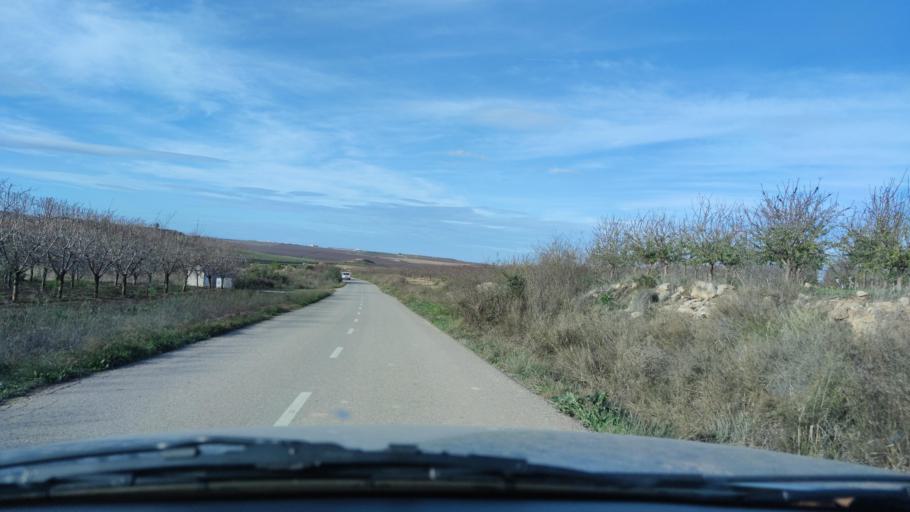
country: ES
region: Catalonia
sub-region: Provincia de Lleida
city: Alcano
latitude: 41.4687
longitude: 0.6423
